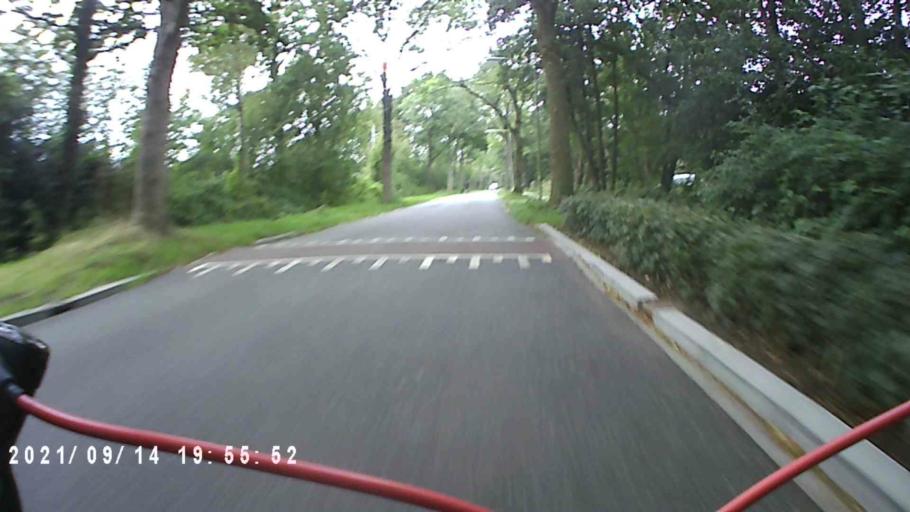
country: NL
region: Groningen
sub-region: Gemeente Haren
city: Haren
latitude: 53.1787
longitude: 6.6098
